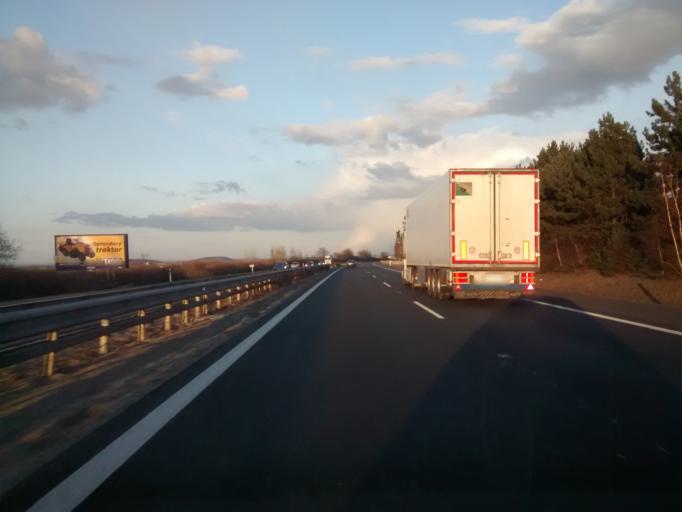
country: CZ
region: Central Bohemia
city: Celakovice
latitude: 50.1324
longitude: 14.7639
